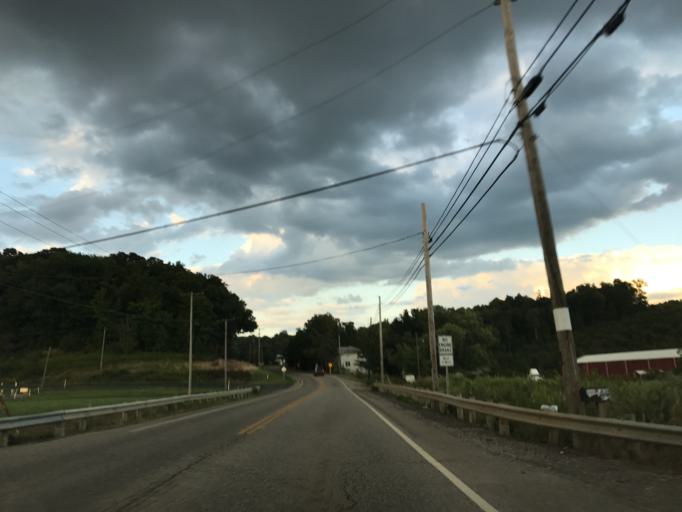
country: US
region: Ohio
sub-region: Stark County
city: Minerva
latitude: 40.7362
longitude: -81.1237
